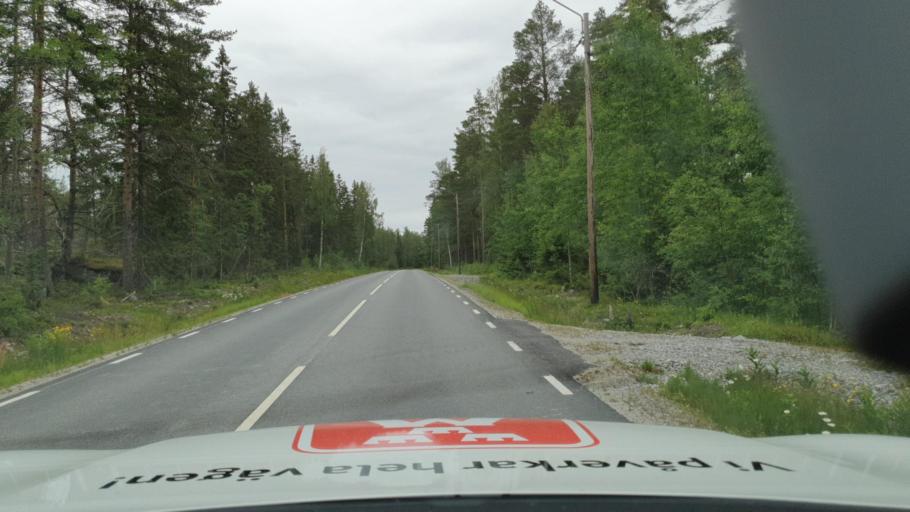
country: SE
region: Vaesterbotten
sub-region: Nordmalings Kommun
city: Nordmaling
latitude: 63.5033
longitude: 19.3299
